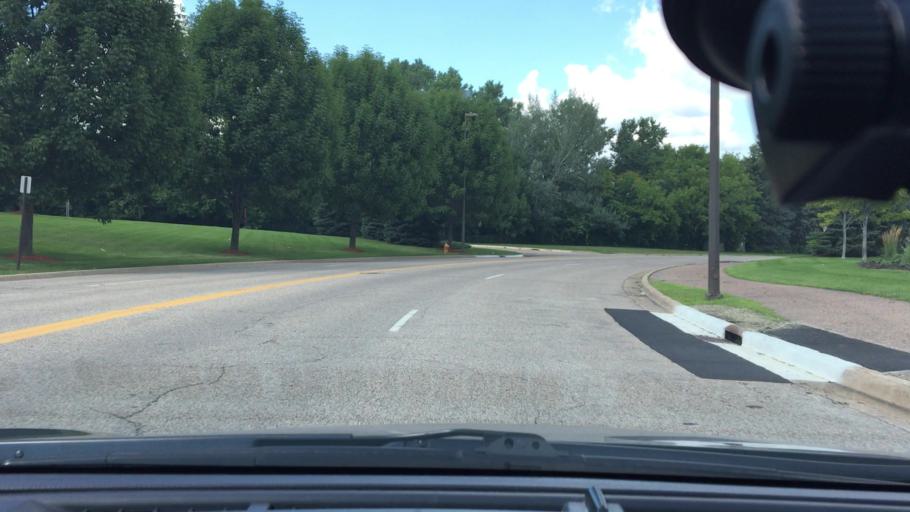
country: US
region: Minnesota
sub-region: Hennepin County
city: Plymouth
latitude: 45.0317
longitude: -93.4493
